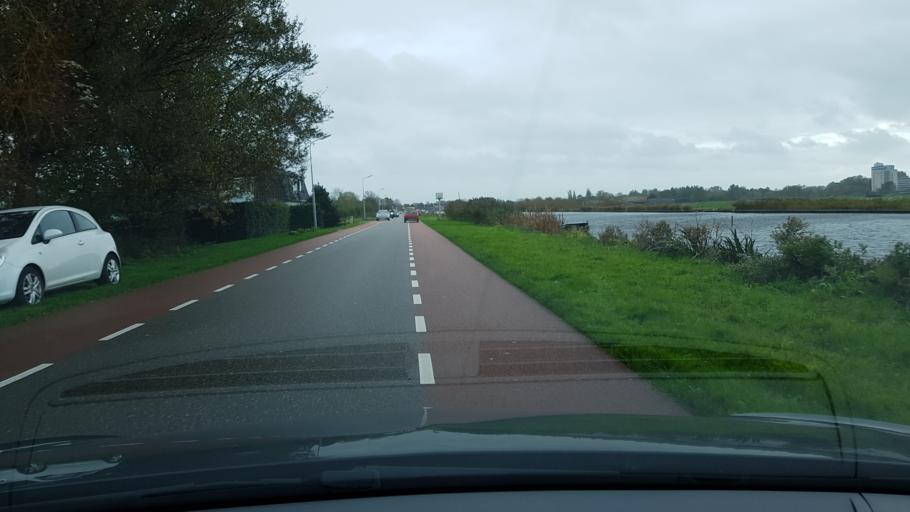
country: NL
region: North Holland
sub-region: Gemeente Haarlem
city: Haarlem
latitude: 52.3630
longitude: 4.6746
